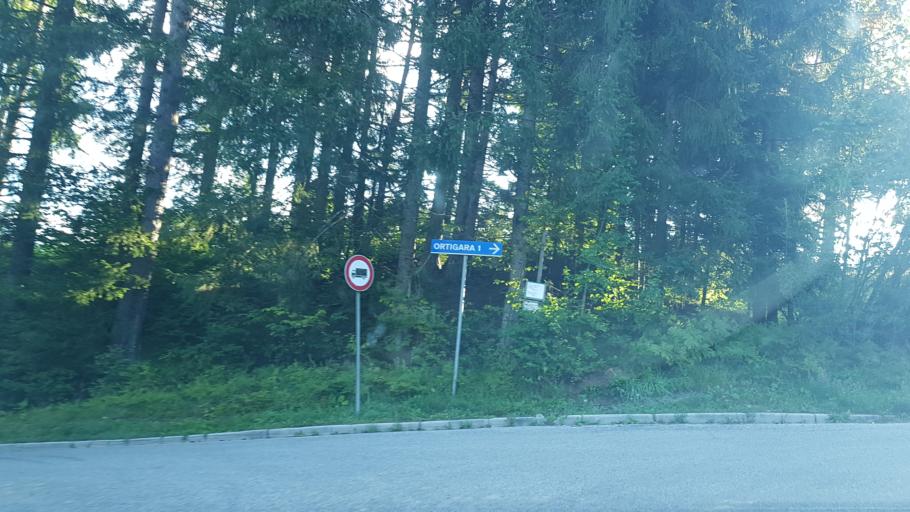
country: IT
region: Friuli Venezia Giulia
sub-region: Provincia di Udine
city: Tarvisio
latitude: 46.4927
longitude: 13.6006
